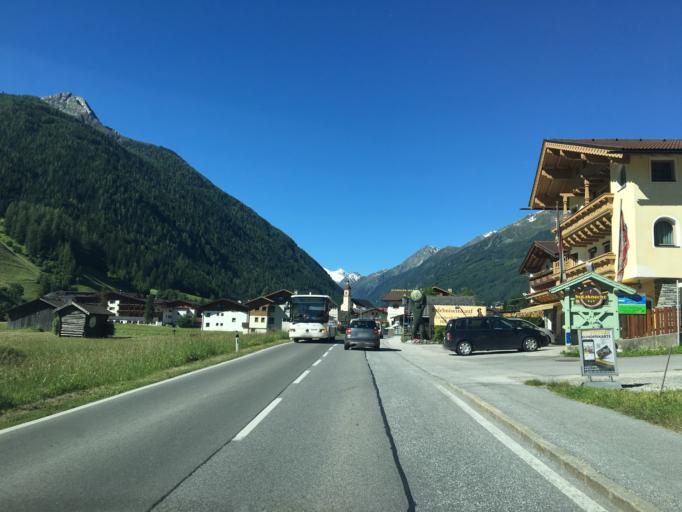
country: AT
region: Tyrol
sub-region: Politischer Bezirk Innsbruck Land
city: Neustift im Stubaital
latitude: 47.1148
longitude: 11.3129
